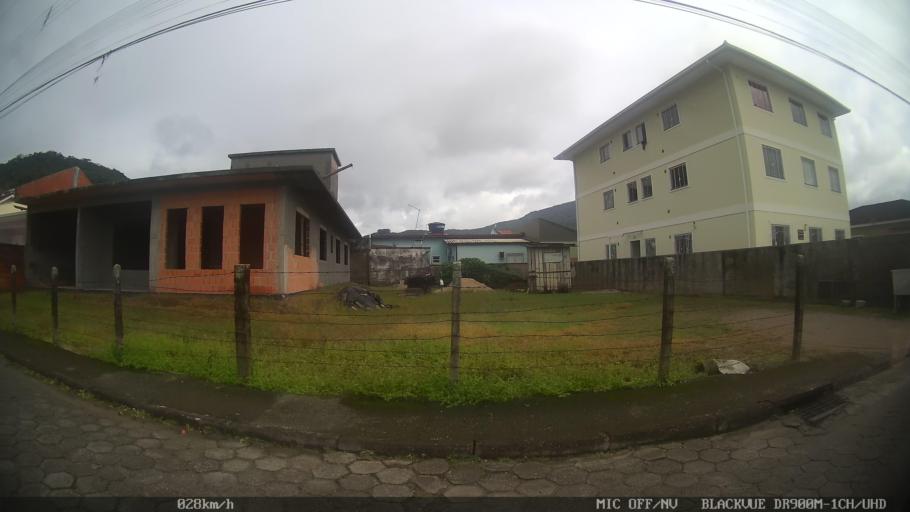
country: BR
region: Santa Catarina
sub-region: Biguacu
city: Biguacu
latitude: -27.5164
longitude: -48.6460
